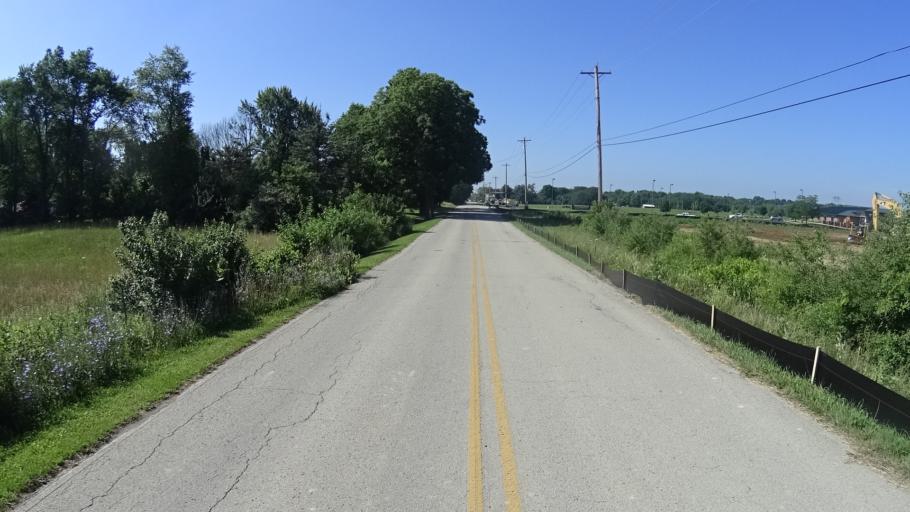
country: US
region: Indiana
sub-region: Madison County
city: Ingalls
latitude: 39.9813
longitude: -85.7962
